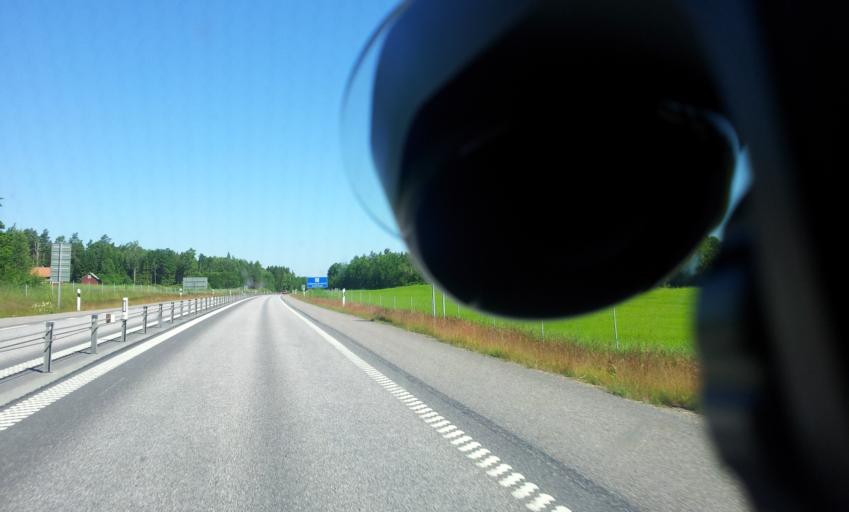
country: SE
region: OEstergoetland
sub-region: Valdemarsviks Kommun
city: Gusum
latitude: 58.3666
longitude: 16.4311
